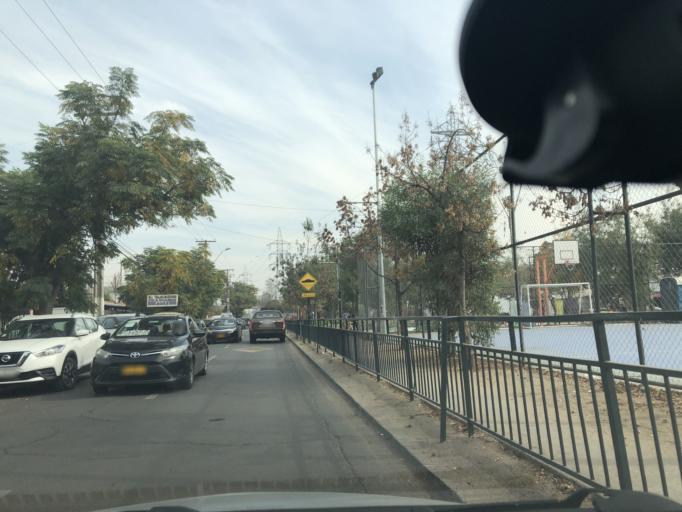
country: CL
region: Santiago Metropolitan
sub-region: Provincia de Cordillera
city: Puente Alto
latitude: -33.5718
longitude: -70.5803
